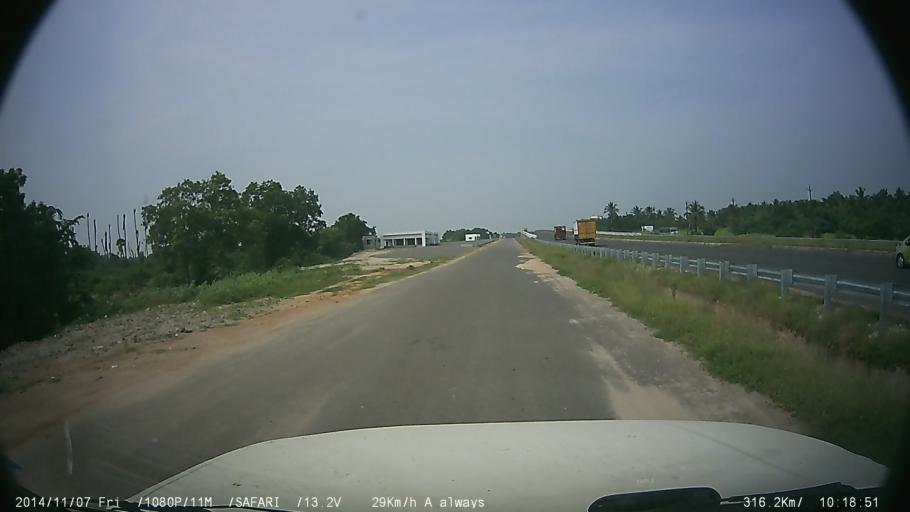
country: IN
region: Tamil Nadu
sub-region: Tiruppur
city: Avinashi
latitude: 11.2003
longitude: 77.3225
